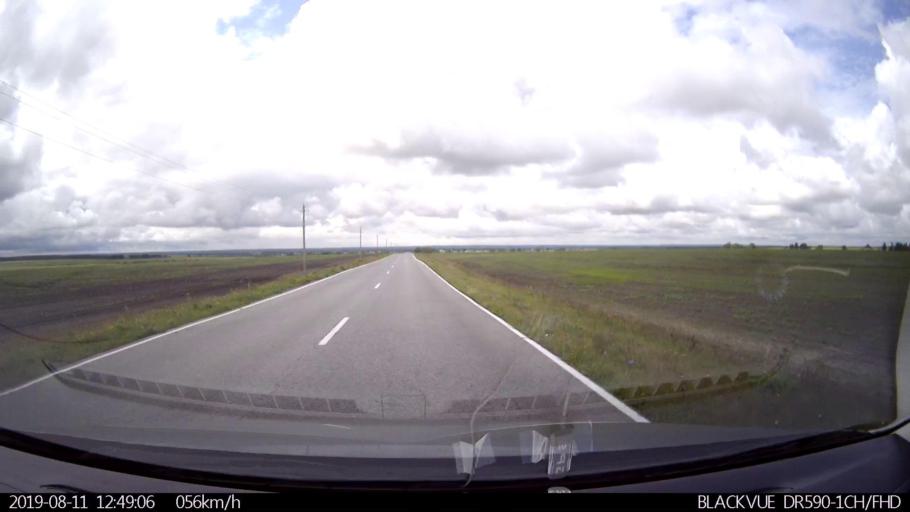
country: RU
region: Ulyanovsk
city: Ignatovka
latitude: 53.8764
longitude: 47.6915
